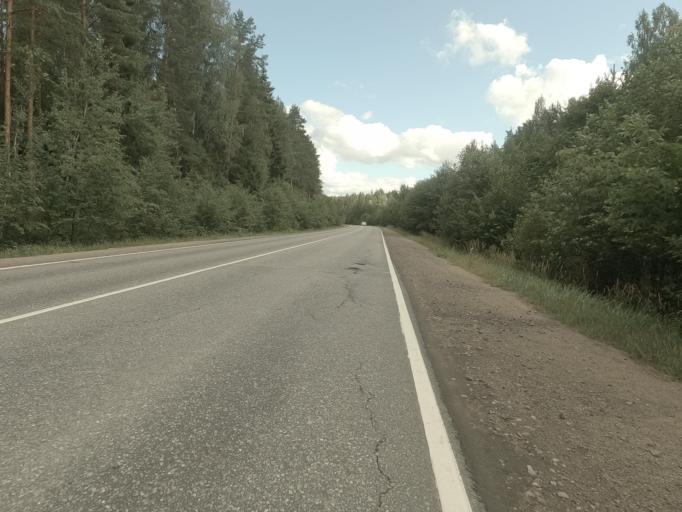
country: RU
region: Leningrad
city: Shcheglovo
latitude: 60.0121
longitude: 30.8548
